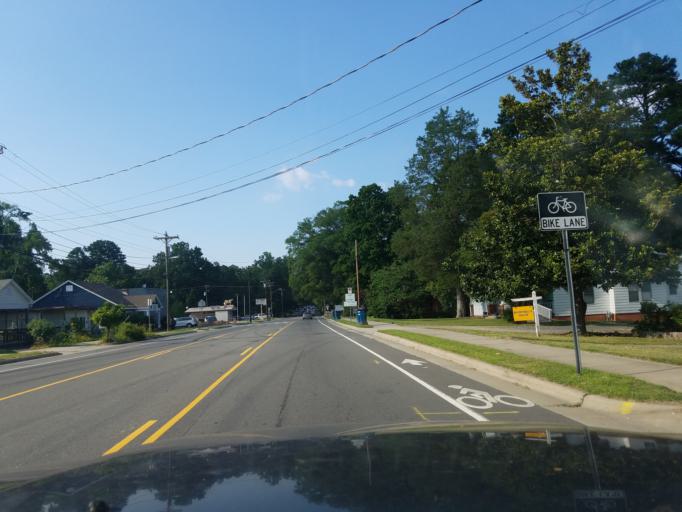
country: US
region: North Carolina
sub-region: Durham County
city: Durham
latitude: 35.9756
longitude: -78.9366
